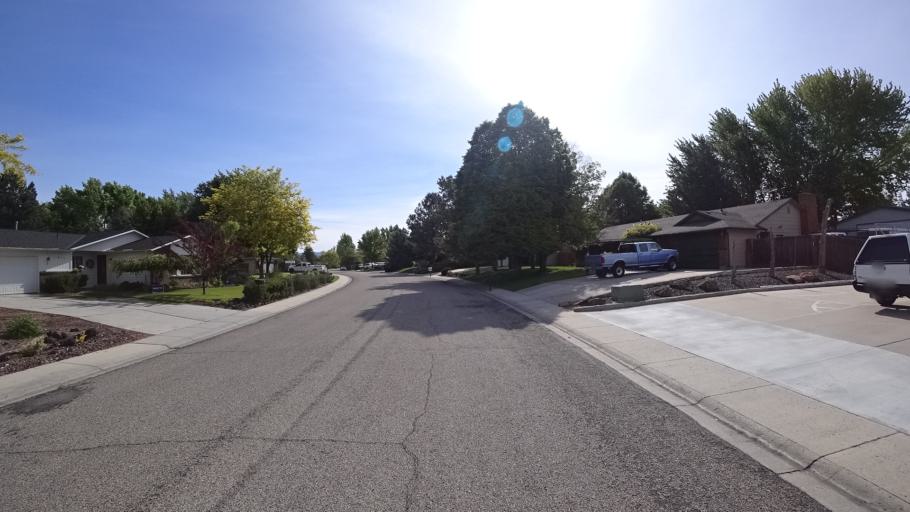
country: US
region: Idaho
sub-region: Ada County
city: Meridian
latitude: 43.5652
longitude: -116.3309
